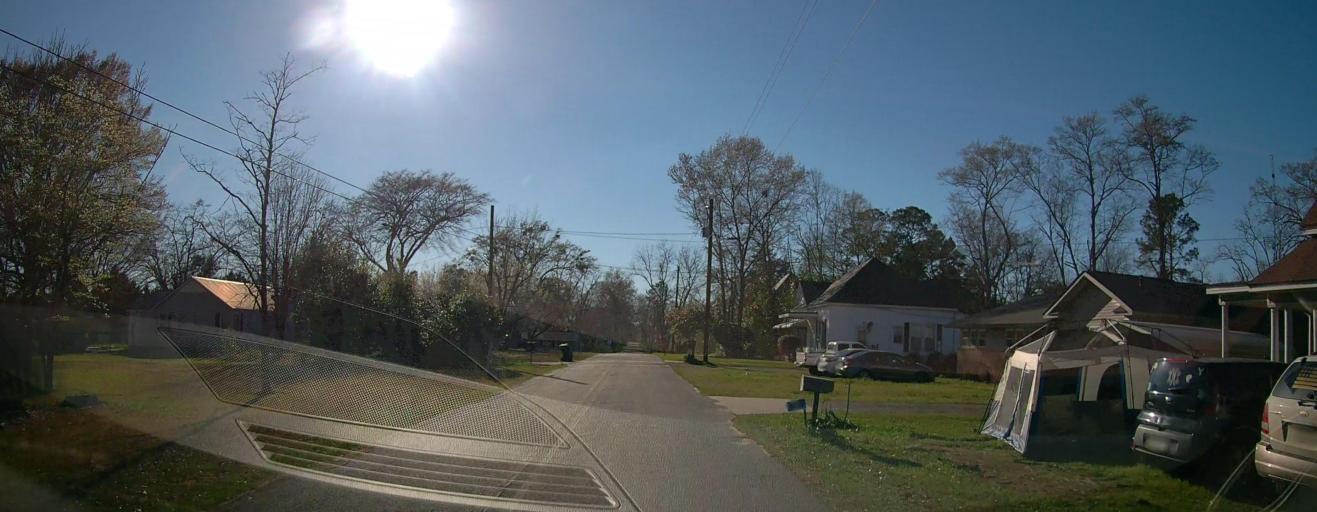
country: US
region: Georgia
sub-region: Taylor County
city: Reynolds
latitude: 32.5550
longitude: -84.0906
